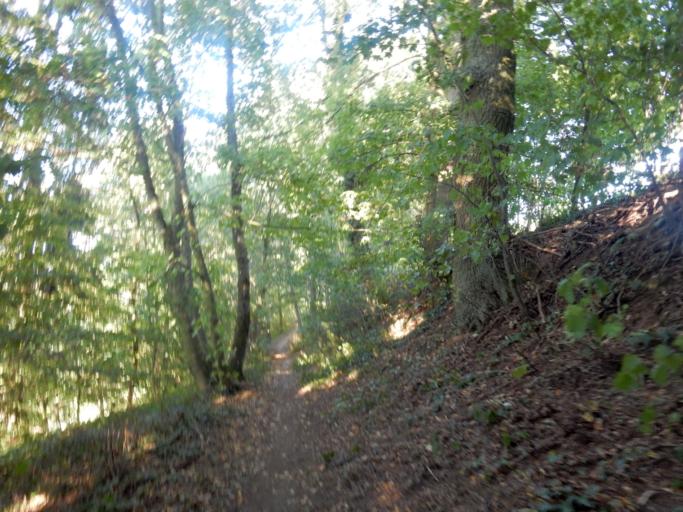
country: LU
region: Luxembourg
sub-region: Canton de Luxembourg
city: Luxembourg
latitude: 49.6048
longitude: 6.1473
